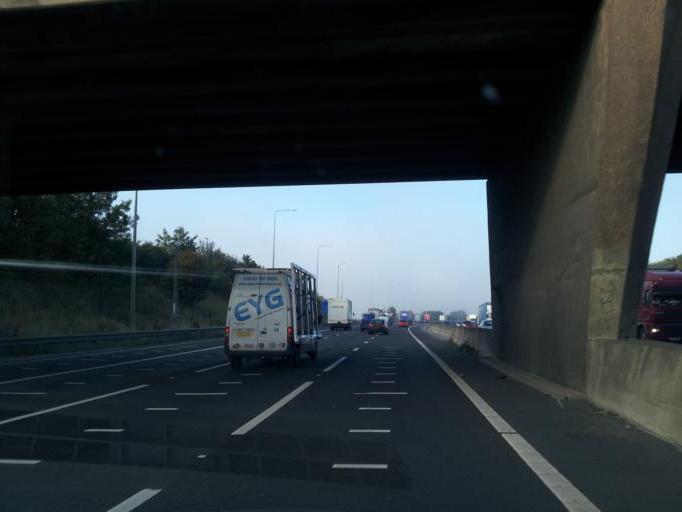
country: GB
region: England
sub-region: City and Borough of Leeds
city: Morley
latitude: 53.7312
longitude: -1.5894
